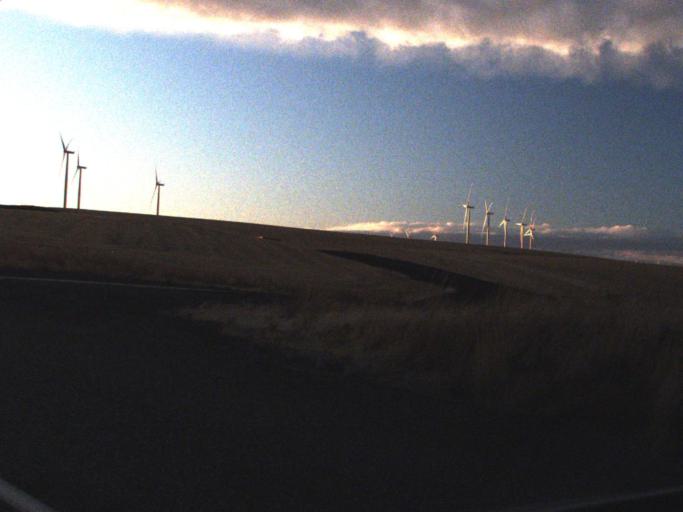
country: US
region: Washington
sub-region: Garfield County
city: Pomeroy
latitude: 46.5258
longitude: -117.7942
